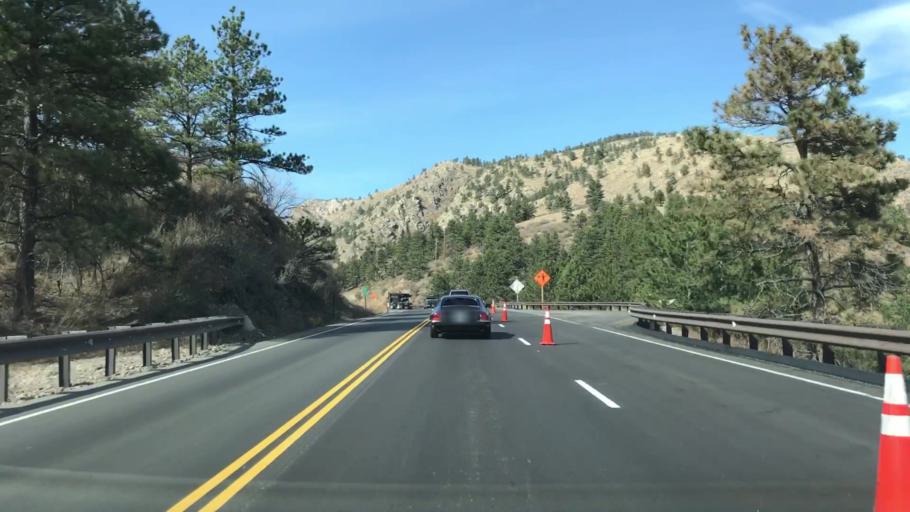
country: US
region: Colorado
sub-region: Boulder County
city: Lyons
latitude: 40.4172
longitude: -105.2699
